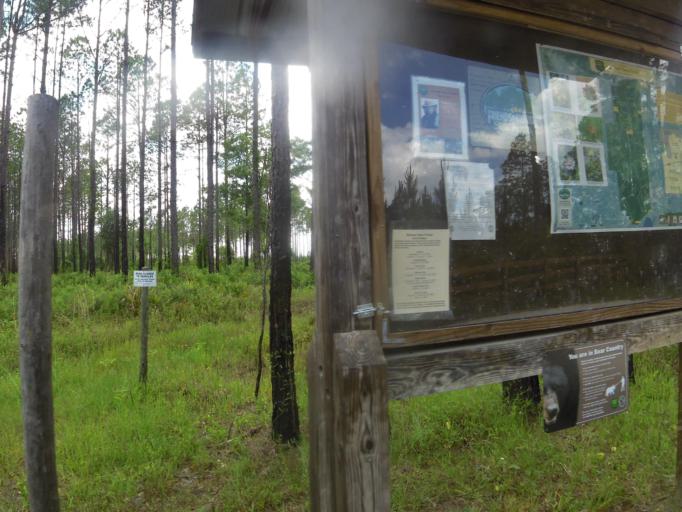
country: US
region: Florida
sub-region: Clay County
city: Asbury Lake
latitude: 29.8968
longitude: -81.8486
